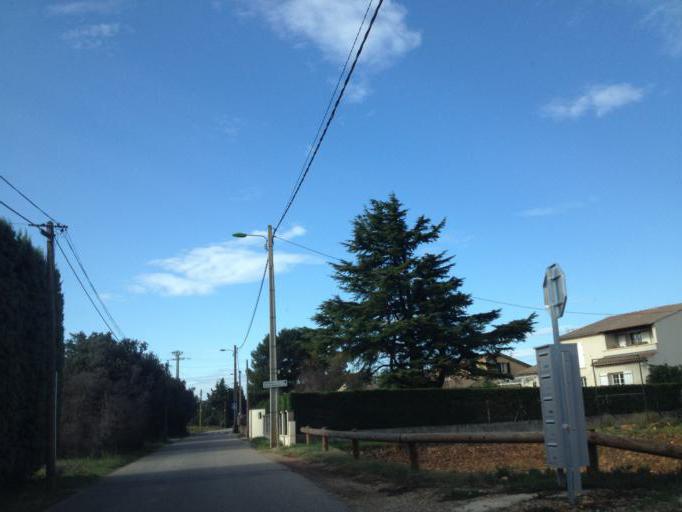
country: FR
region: Provence-Alpes-Cote d'Azur
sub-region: Departement du Vaucluse
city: Sorgues
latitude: 44.0335
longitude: 4.8692
